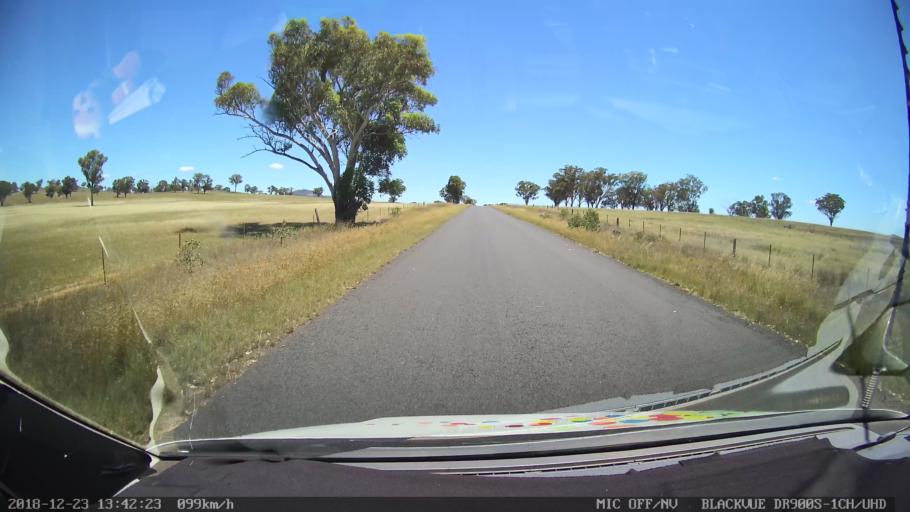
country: AU
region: New South Wales
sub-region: Armidale Dumaresq
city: Armidale
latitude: -30.4764
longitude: 151.1632
